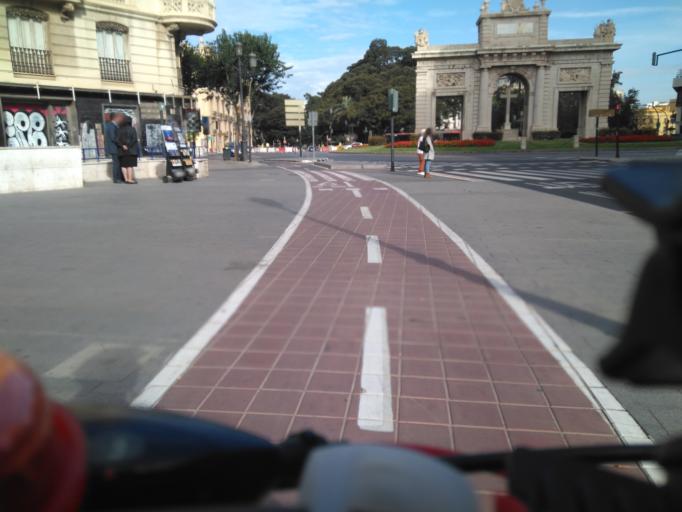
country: ES
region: Valencia
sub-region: Provincia de Valencia
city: Valencia
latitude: 39.4718
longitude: -0.3677
